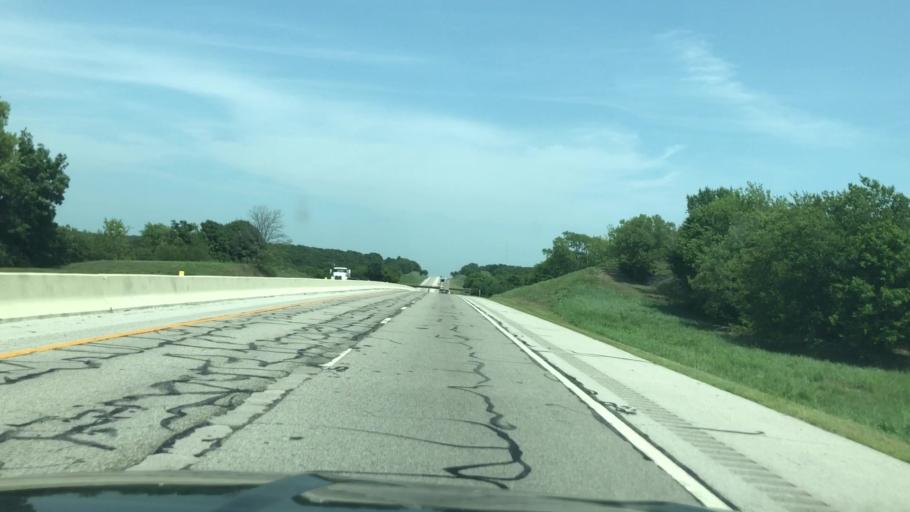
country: US
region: Oklahoma
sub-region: Rogers County
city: Chelsea
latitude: 36.4602
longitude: -95.3501
